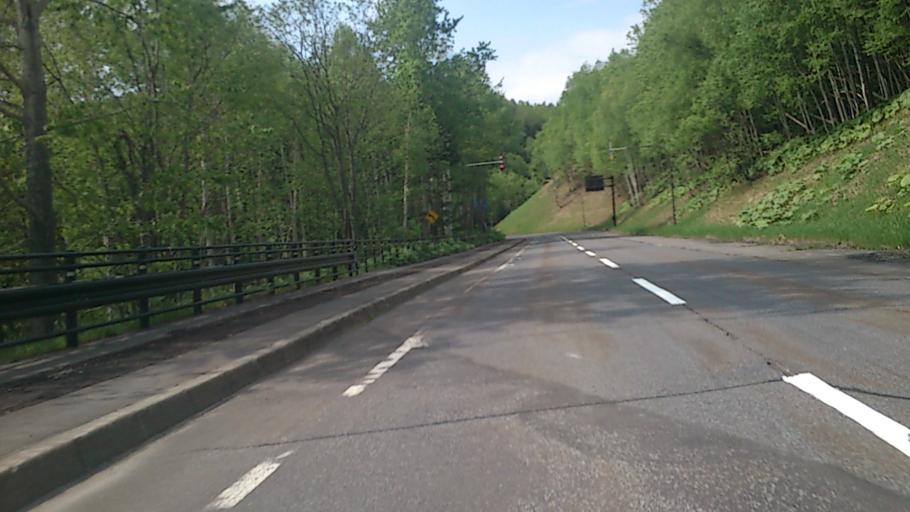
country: JP
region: Hokkaido
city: Kamikawa
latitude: 43.6642
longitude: 143.0356
